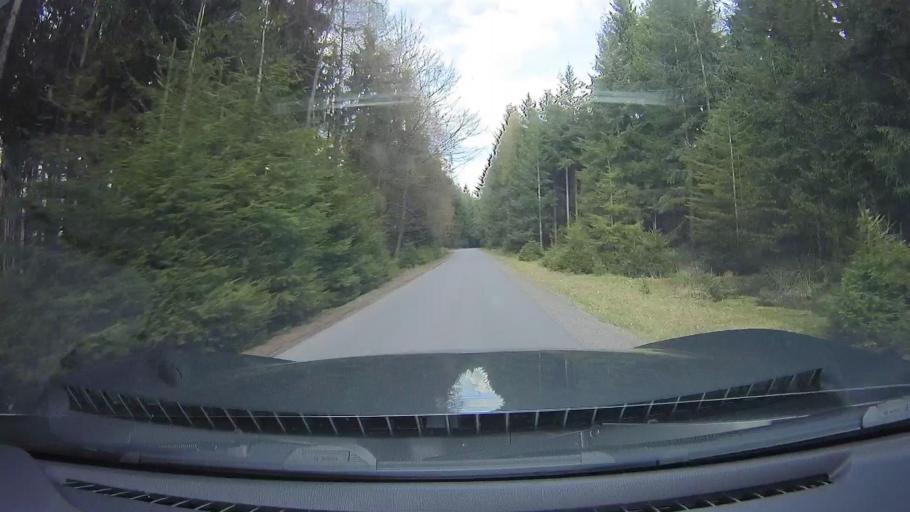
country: DE
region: Hesse
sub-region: Regierungsbezirk Darmstadt
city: Hesseneck
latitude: 49.6059
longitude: 9.0792
